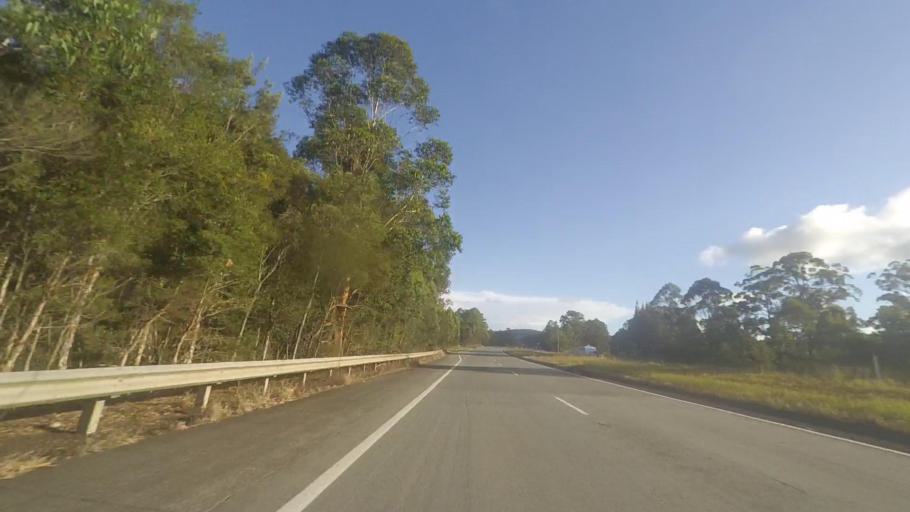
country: AU
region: New South Wales
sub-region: Great Lakes
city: Nabiac
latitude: -32.2474
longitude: 152.3225
